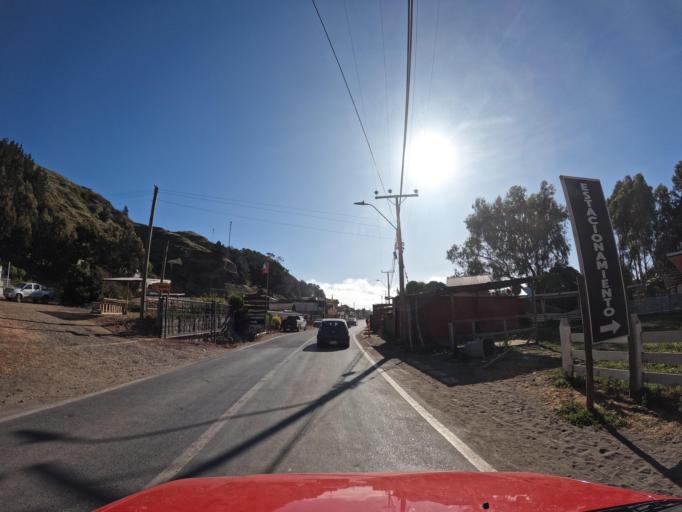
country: CL
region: Maule
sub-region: Provincia de Talca
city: Constitucion
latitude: -34.8849
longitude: -72.1610
